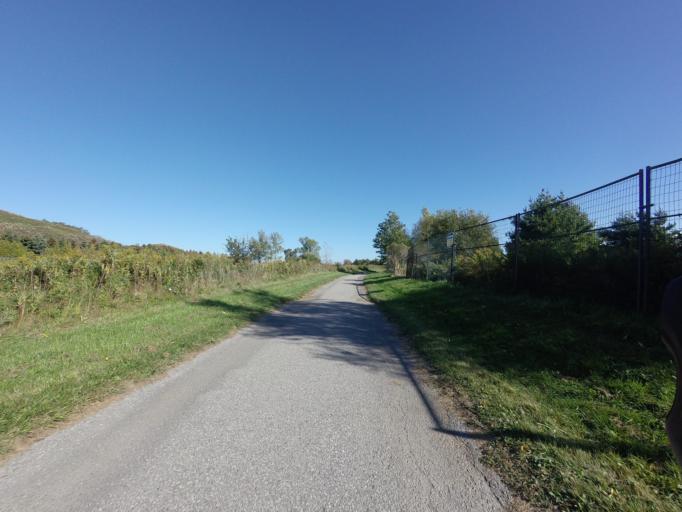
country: CA
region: Ontario
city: Oshawa
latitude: 43.8473
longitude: -78.9094
